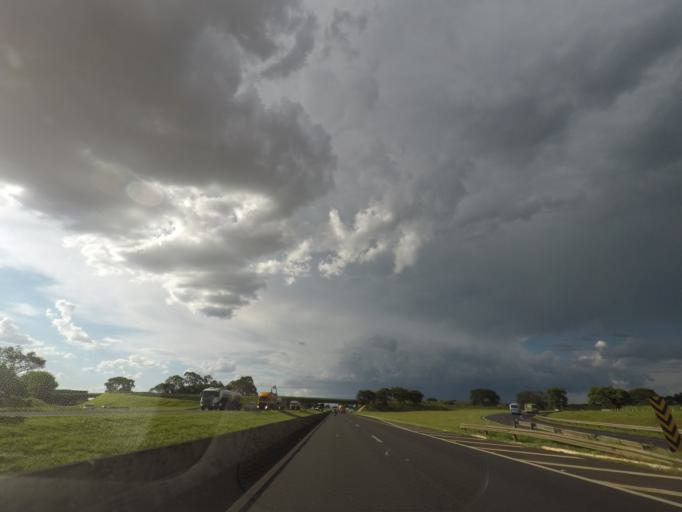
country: BR
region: Sao Paulo
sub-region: Ribeirao Preto
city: Ribeirao Preto
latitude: -21.1156
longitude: -47.7781
